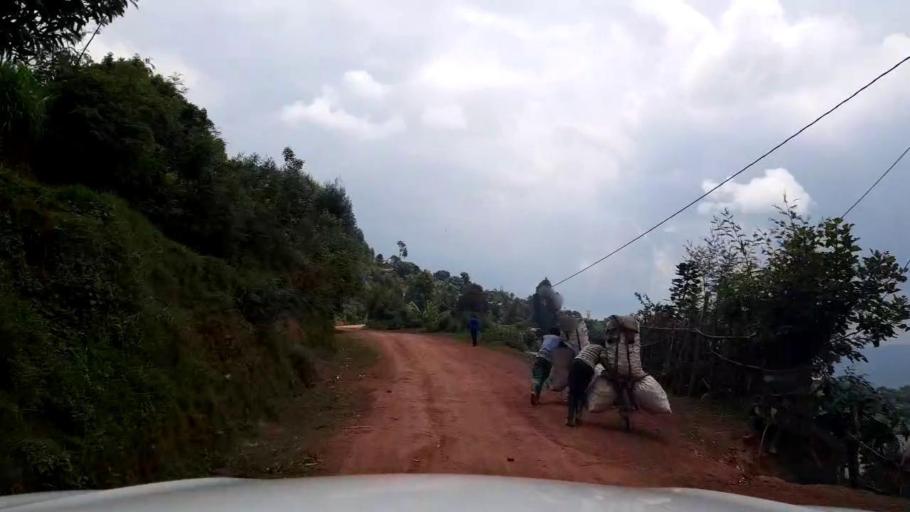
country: RW
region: Northern Province
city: Byumba
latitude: -1.4890
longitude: 29.9291
